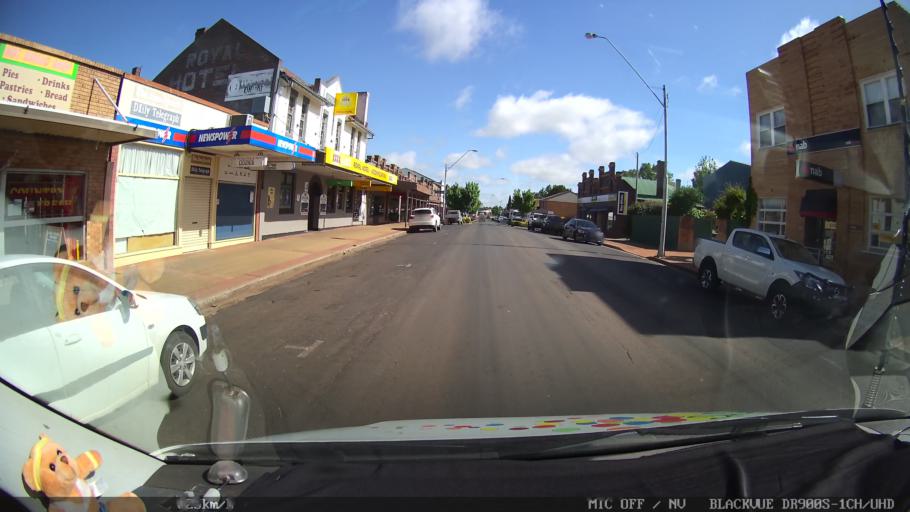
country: AU
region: New South Wales
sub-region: Guyra
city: Guyra
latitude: -30.2191
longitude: 151.6717
